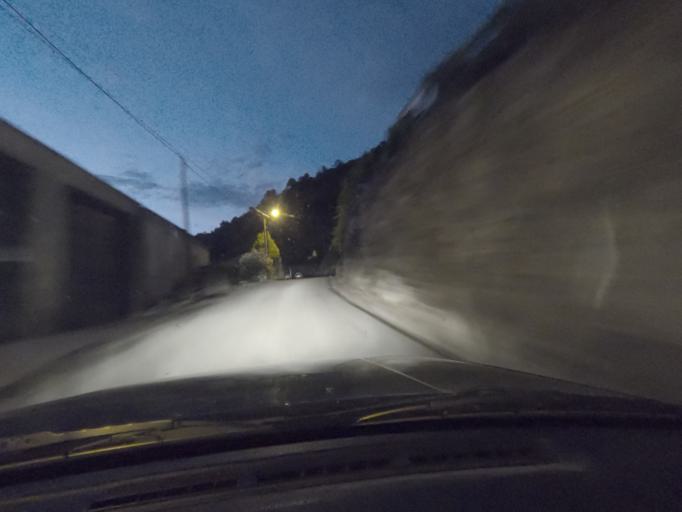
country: PT
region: Vila Real
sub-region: Peso da Regua
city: Godim
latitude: 41.1823
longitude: -7.8335
